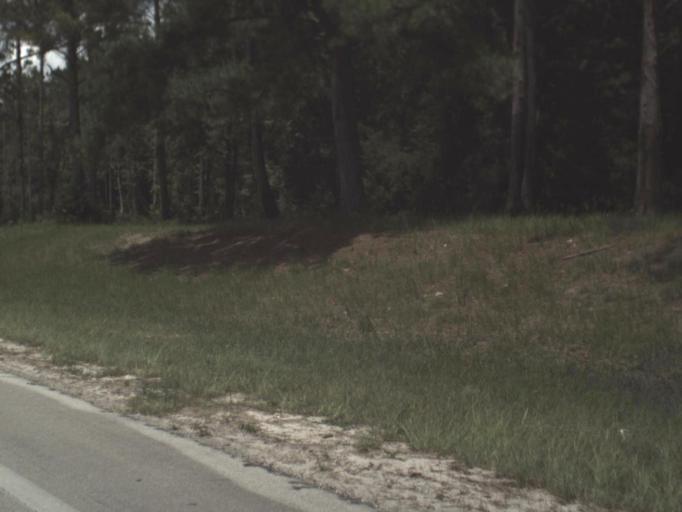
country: US
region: Florida
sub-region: Alachua County
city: High Springs
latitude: 29.7862
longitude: -82.6080
